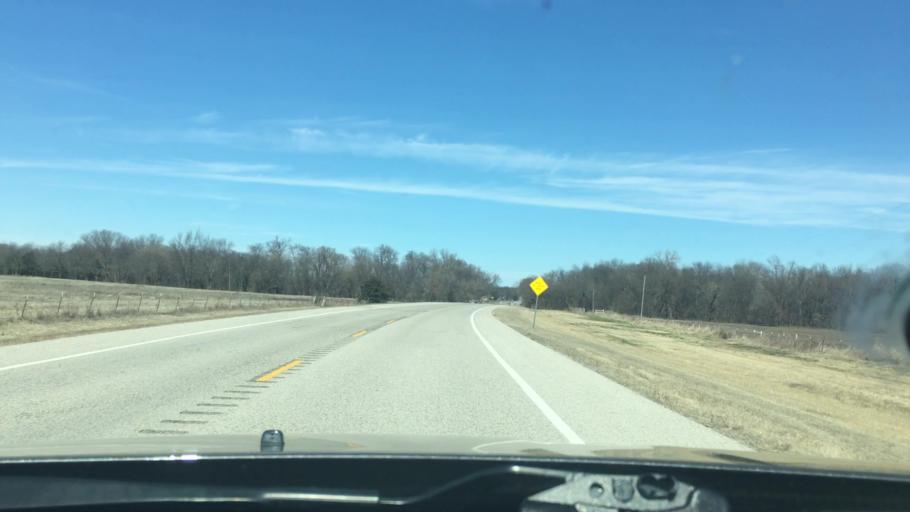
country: US
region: Oklahoma
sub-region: Murray County
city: Sulphur
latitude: 34.3873
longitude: -96.9510
